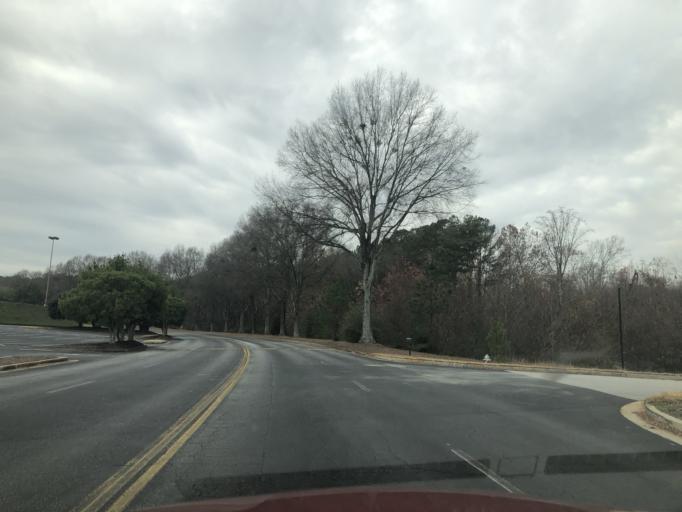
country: US
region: Georgia
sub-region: Clayton County
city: Morrow
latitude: 33.5770
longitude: -84.3543
